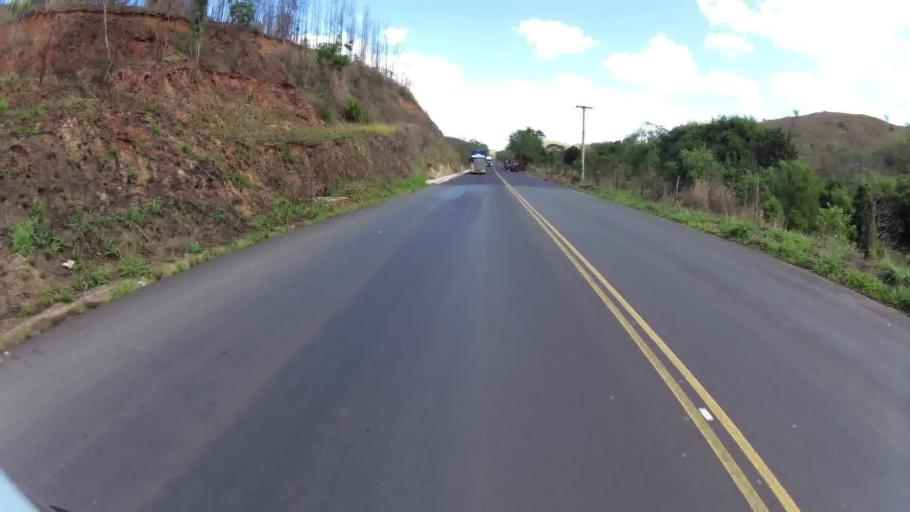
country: BR
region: Rio de Janeiro
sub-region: Itaperuna
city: Itaperuna
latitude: -21.3403
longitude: -41.8964
